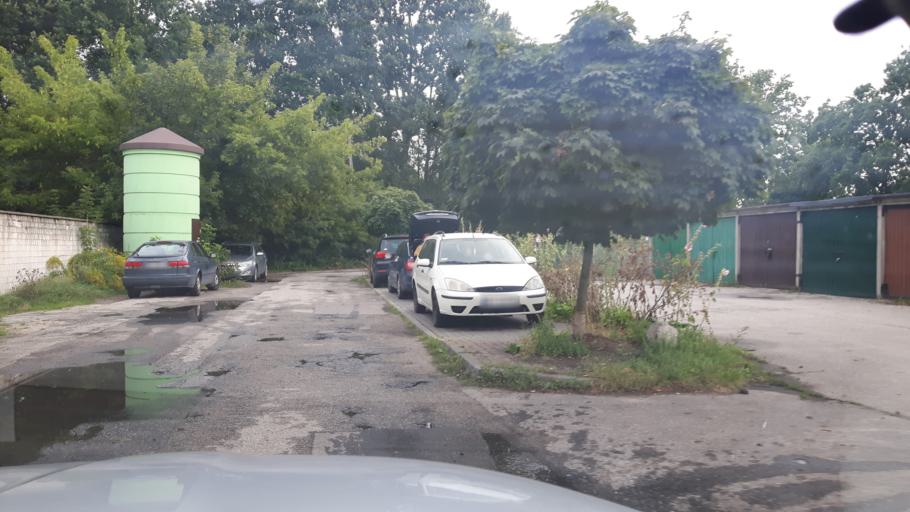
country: PL
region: Masovian Voivodeship
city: Zielonka
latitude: 52.3157
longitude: 21.1641
